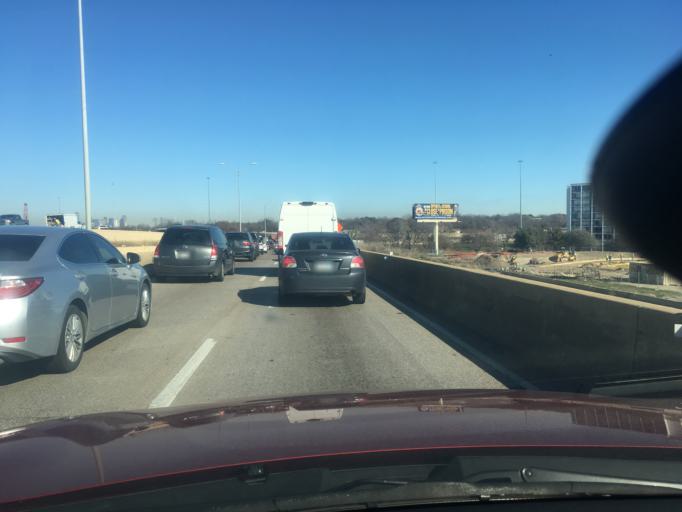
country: US
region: Texas
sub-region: Dallas County
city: Cockrell Hill
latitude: 32.7052
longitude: -96.8318
